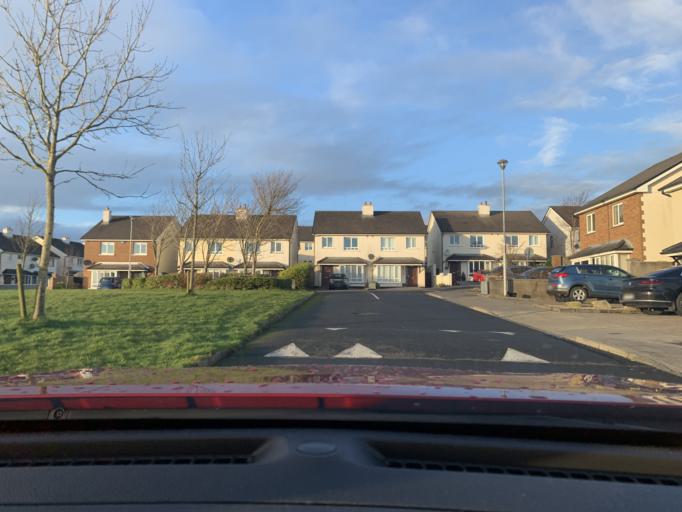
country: IE
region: Connaught
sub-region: Sligo
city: Sligo
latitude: 54.2501
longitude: -8.4674
